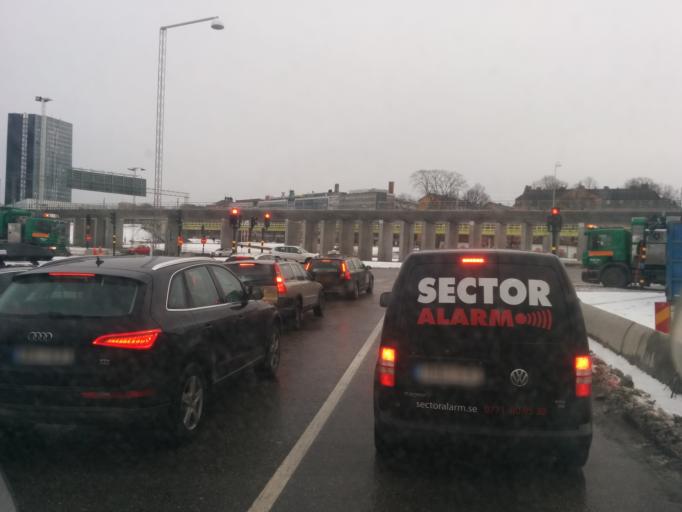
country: SE
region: Stockholm
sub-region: Stockholms Kommun
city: Stockholm
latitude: 59.3512
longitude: 18.0412
